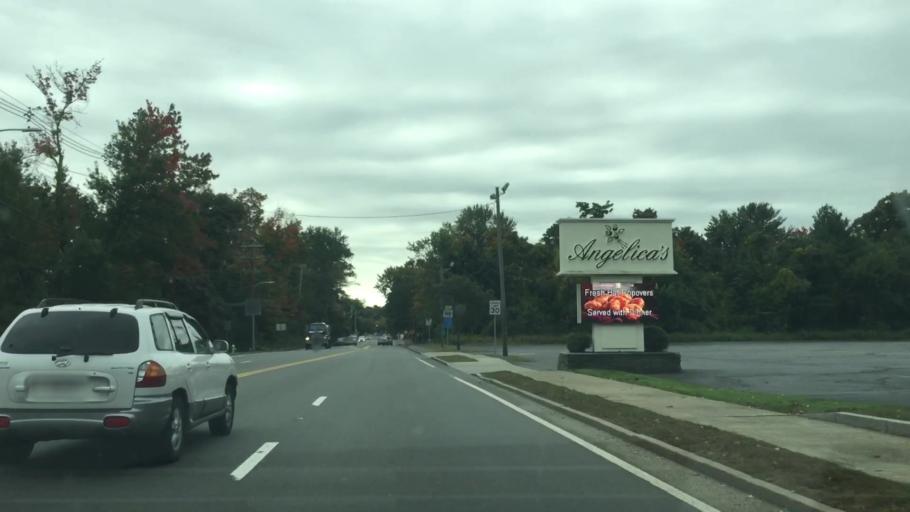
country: US
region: Massachusetts
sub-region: Essex County
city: Middleton
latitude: 42.5929
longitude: -71.0150
